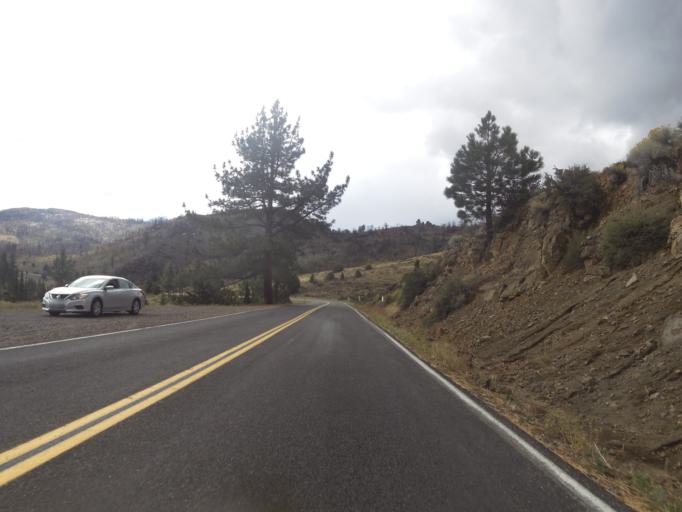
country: US
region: Nevada
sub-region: Douglas County
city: Gardnerville Ranchos
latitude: 38.6717
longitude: -119.6650
